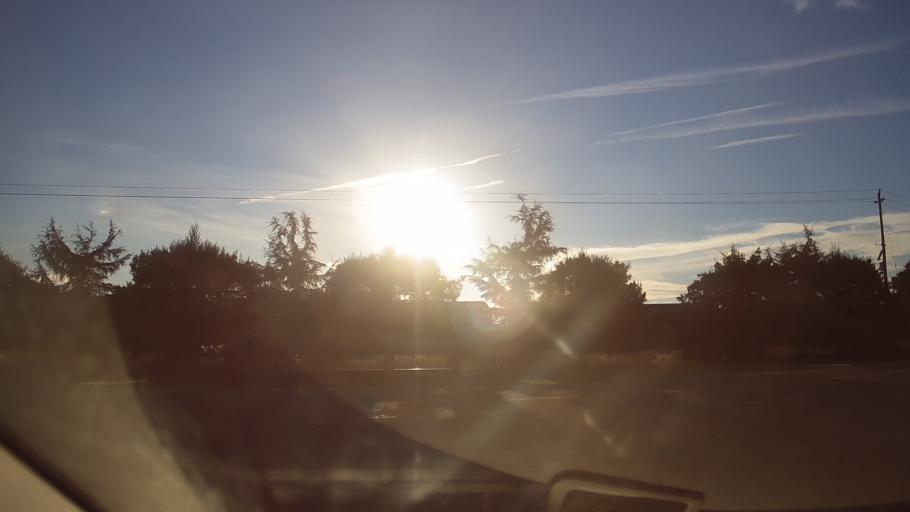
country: US
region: California
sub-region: Yolo County
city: West Sacramento
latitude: 38.5729
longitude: -121.5545
